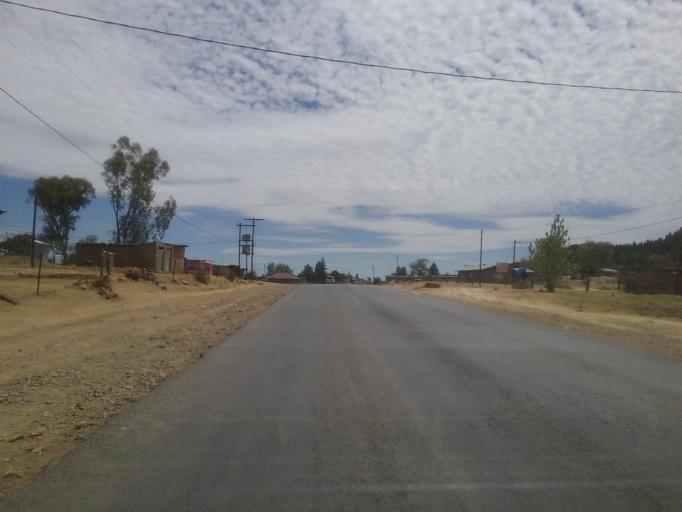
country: LS
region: Mafeteng
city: Mafeteng
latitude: -29.8374
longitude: 27.2328
